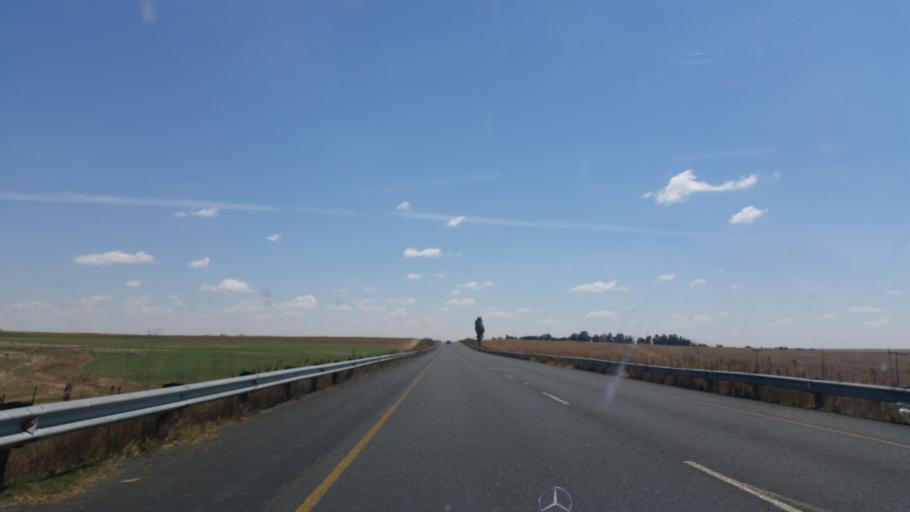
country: ZA
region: Orange Free State
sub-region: Thabo Mofutsanyana District Municipality
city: Bethlehem
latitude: -28.1119
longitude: 28.6721
